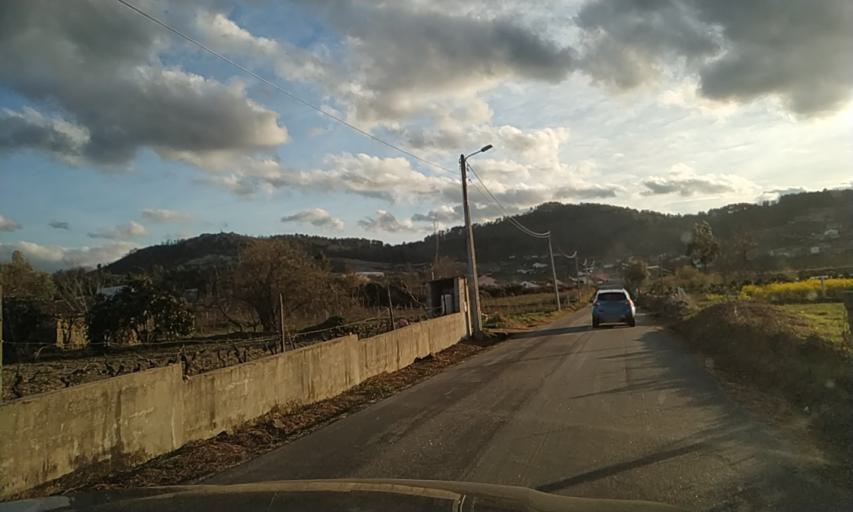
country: PT
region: Braganca
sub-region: Carrazeda de Ansiaes
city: Carrazeda de Anciaes
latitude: 41.2249
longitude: -7.3396
